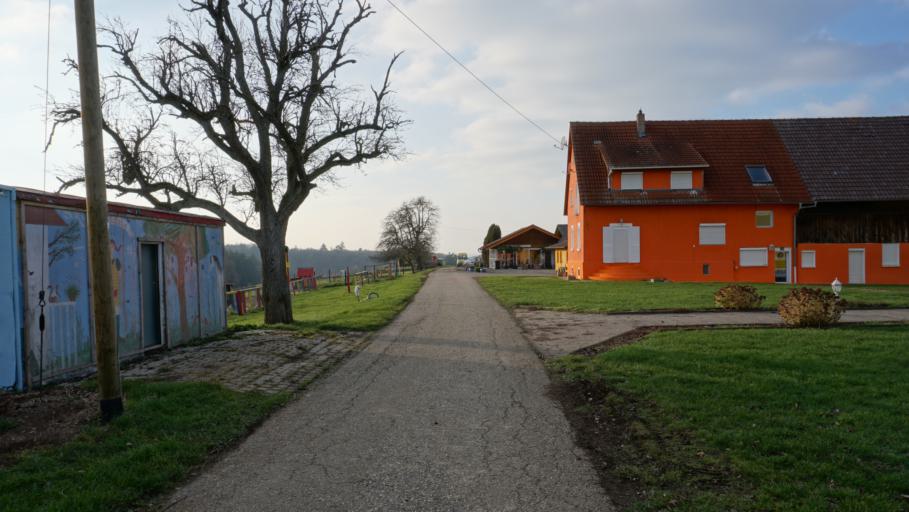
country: DE
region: Baden-Wuerttemberg
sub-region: Karlsruhe Region
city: Huffenhardt
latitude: 49.3042
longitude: 9.0643
